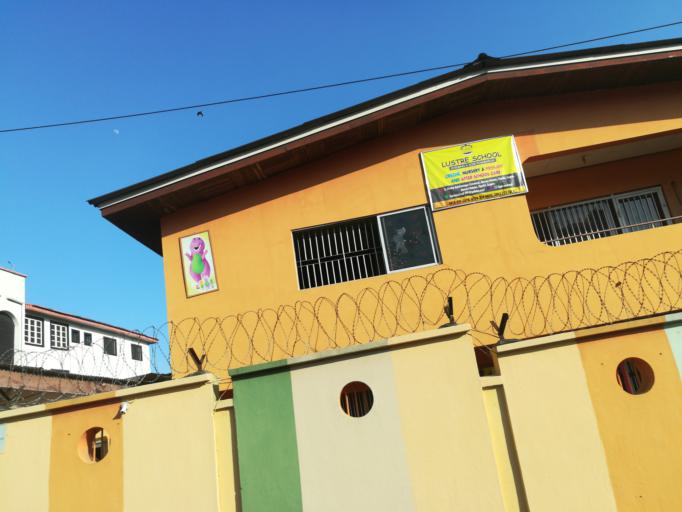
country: NG
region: Lagos
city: Ojota
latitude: 6.5834
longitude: 3.3671
